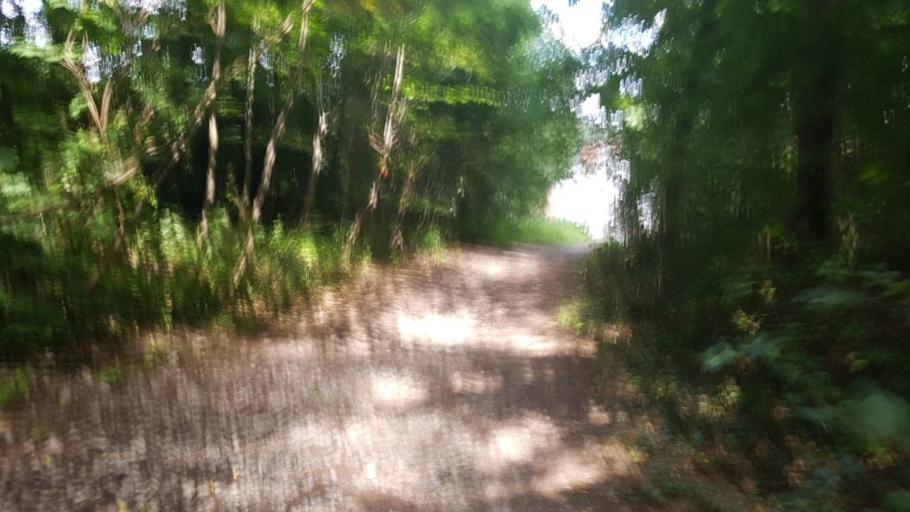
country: BE
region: Wallonia
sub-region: Province du Hainaut
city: Charleroi
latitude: 50.3498
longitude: 4.4069
